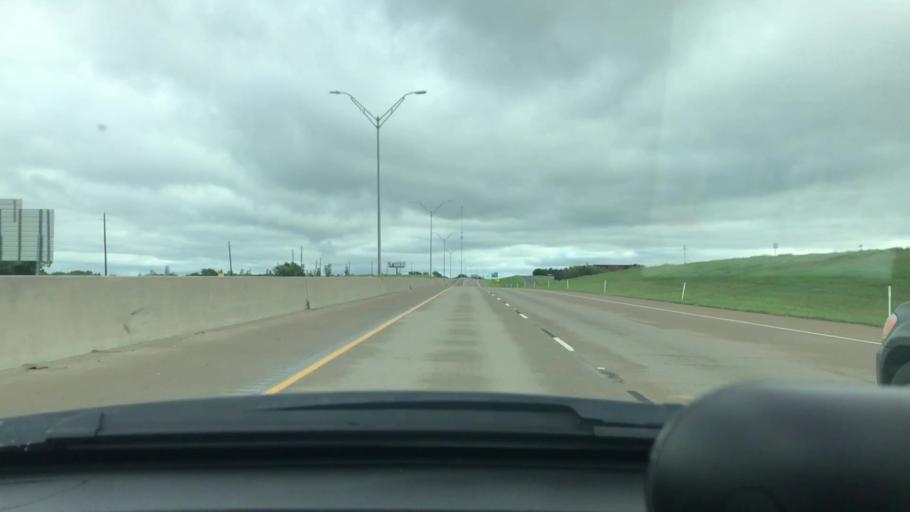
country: US
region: Texas
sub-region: Grayson County
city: Howe
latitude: 33.5165
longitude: -96.6157
